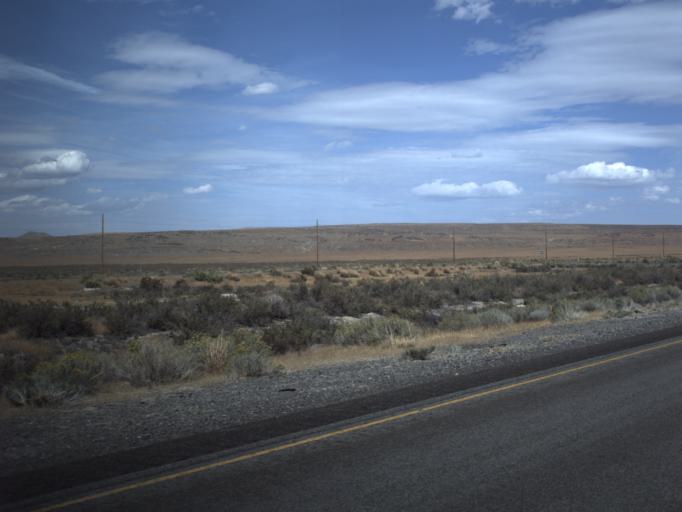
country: US
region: Utah
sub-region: Tooele County
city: Grantsville
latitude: 40.7469
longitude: -113.0576
